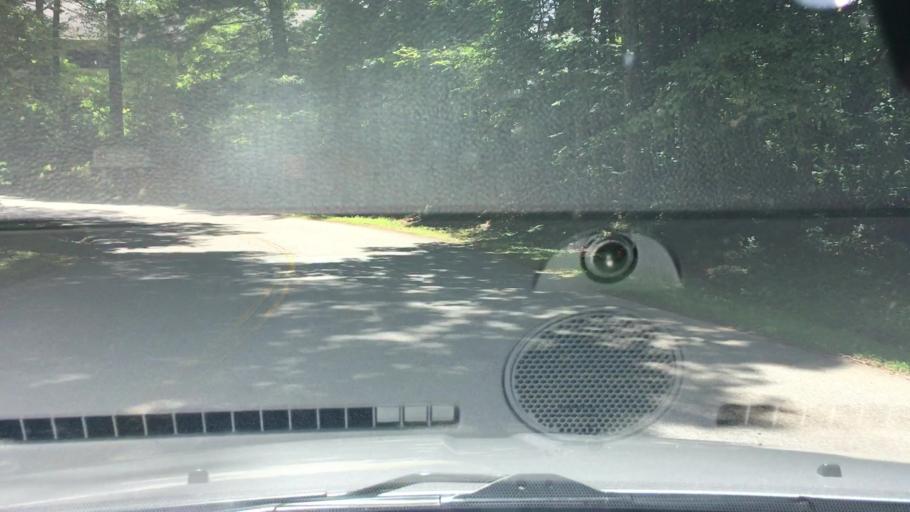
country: US
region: North Carolina
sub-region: Buncombe County
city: Asheville
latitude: 35.5935
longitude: -82.4821
